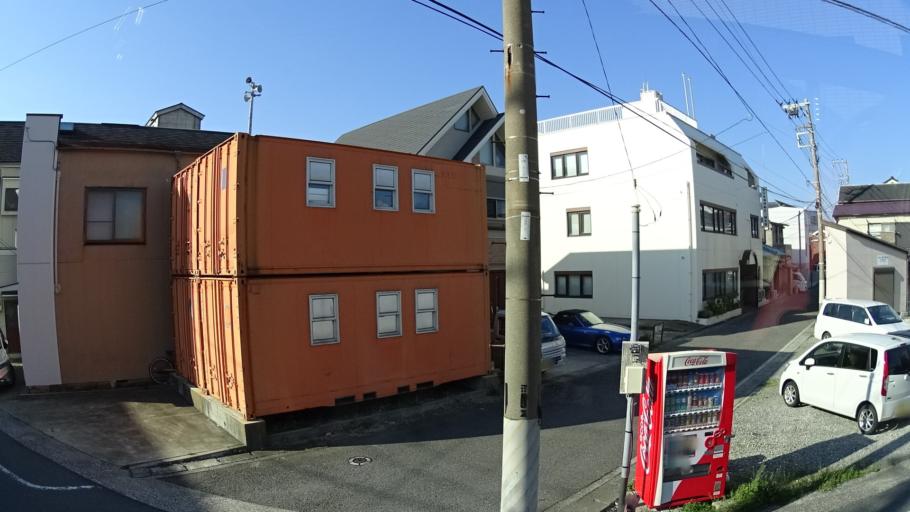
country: JP
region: Kanagawa
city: Miura
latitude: 35.1394
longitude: 139.6191
